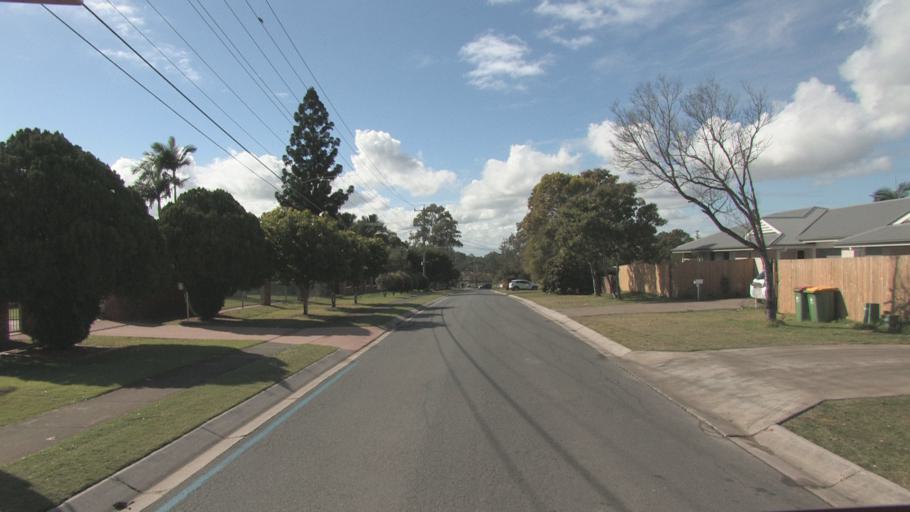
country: AU
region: Queensland
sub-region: Logan
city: Waterford West
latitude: -27.6831
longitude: 153.1227
